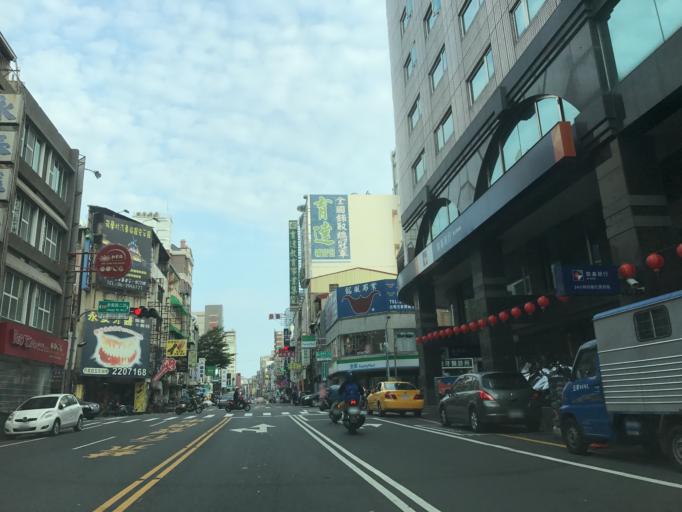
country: TW
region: Taiwan
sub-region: Tainan
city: Tainan
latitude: 22.9964
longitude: 120.2036
